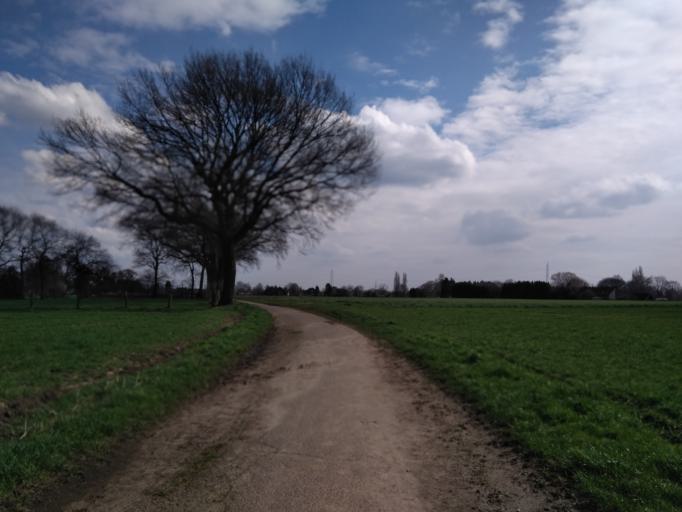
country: DE
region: North Rhine-Westphalia
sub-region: Regierungsbezirk Munster
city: Gladbeck
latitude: 51.5823
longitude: 7.0094
